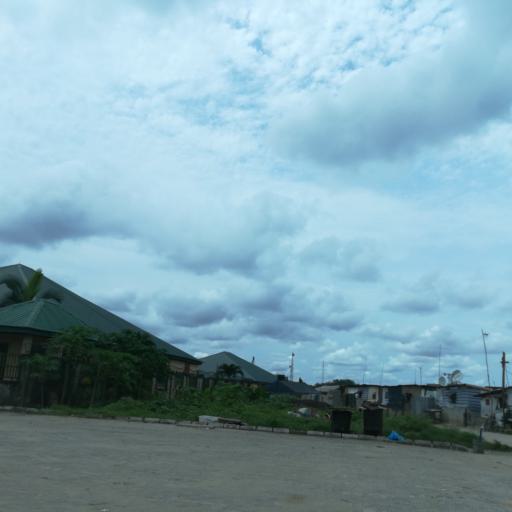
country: NG
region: Rivers
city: Port Harcourt
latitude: 4.7929
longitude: 7.0256
